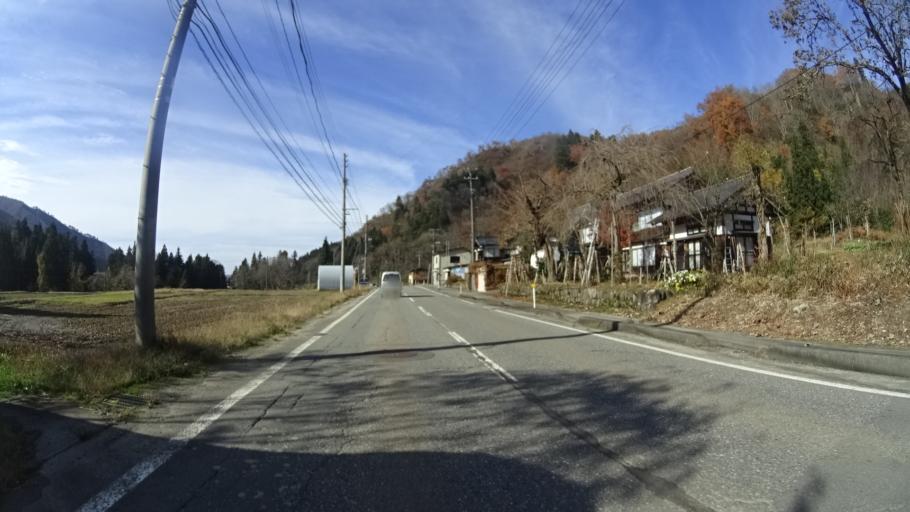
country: JP
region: Niigata
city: Muikamachi
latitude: 37.2240
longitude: 139.0229
